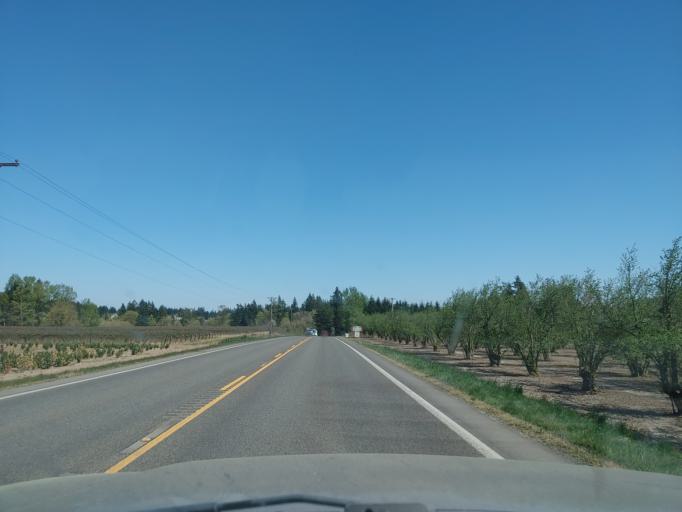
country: US
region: Oregon
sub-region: Yamhill County
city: Newberg
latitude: 45.2342
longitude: -122.8998
